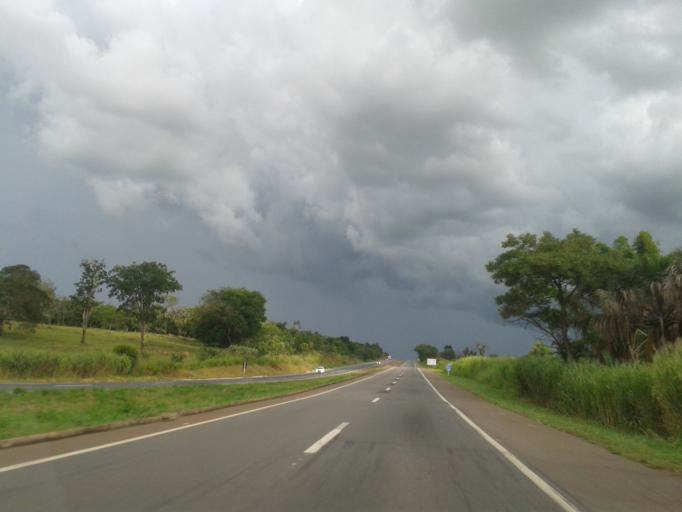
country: BR
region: Goias
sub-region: Morrinhos
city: Morrinhos
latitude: -17.5346
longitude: -49.2132
